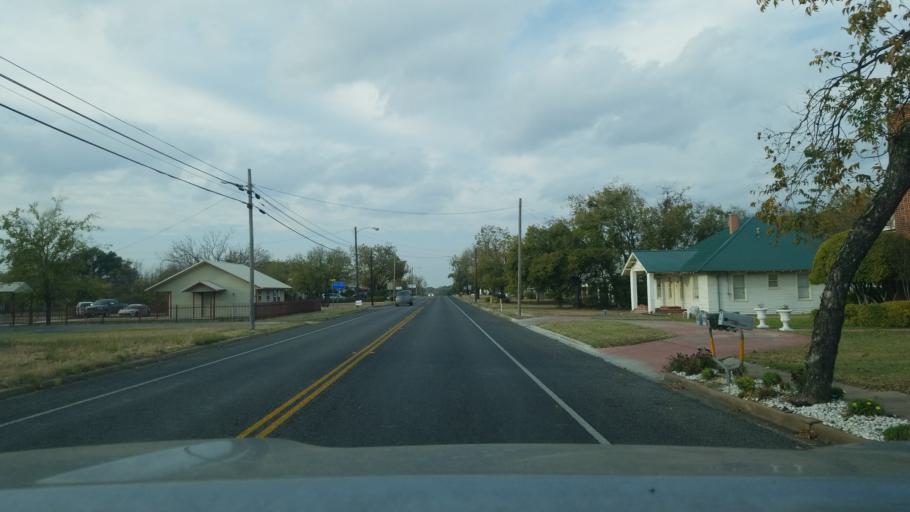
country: US
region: Texas
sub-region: Mills County
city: Goldthwaite
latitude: 31.4581
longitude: -98.5725
